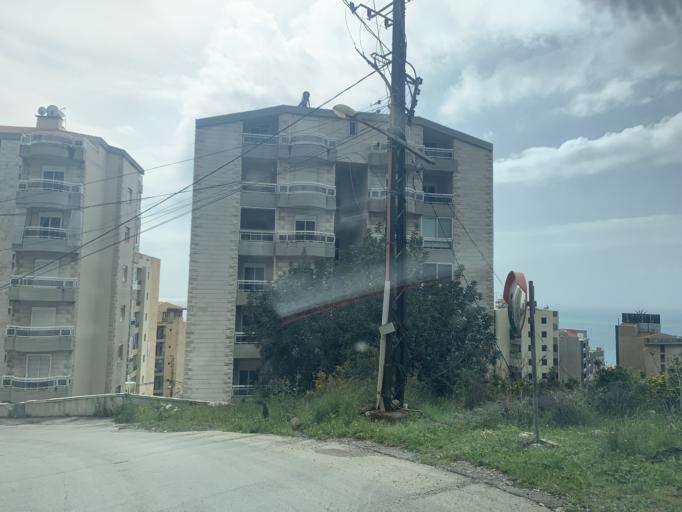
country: LB
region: Mont-Liban
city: Djounie
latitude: 34.0032
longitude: 35.6522
